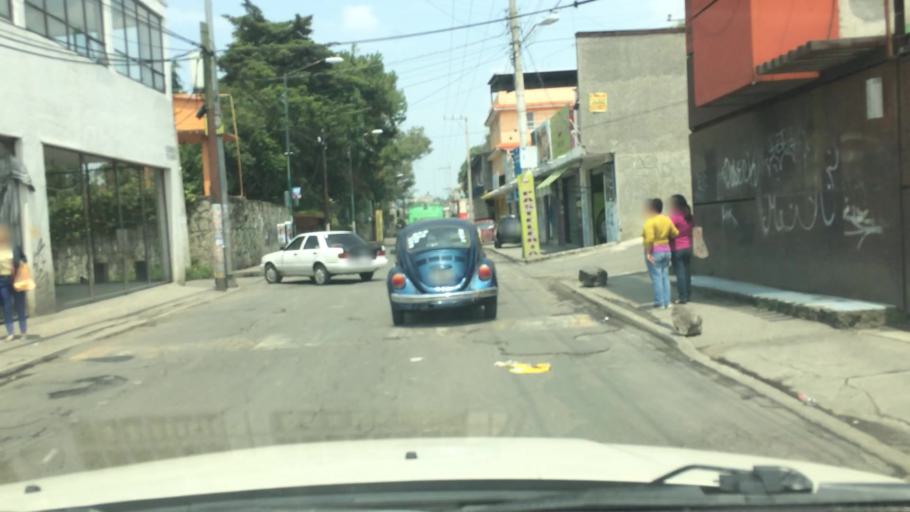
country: MX
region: Mexico City
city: Tlalpan
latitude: 19.2345
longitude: -99.1684
